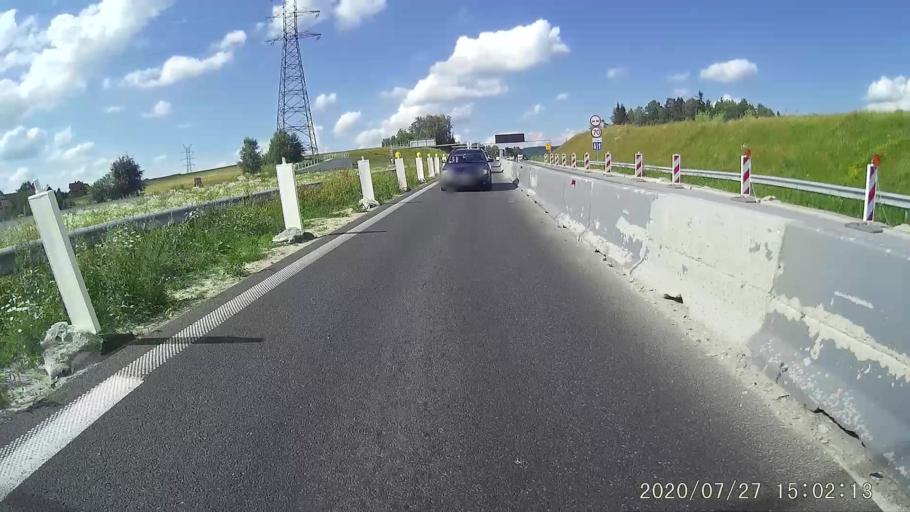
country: PL
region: Lesser Poland Voivodeship
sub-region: Powiat suski
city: Naprawa
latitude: 49.6739
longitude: 19.8879
